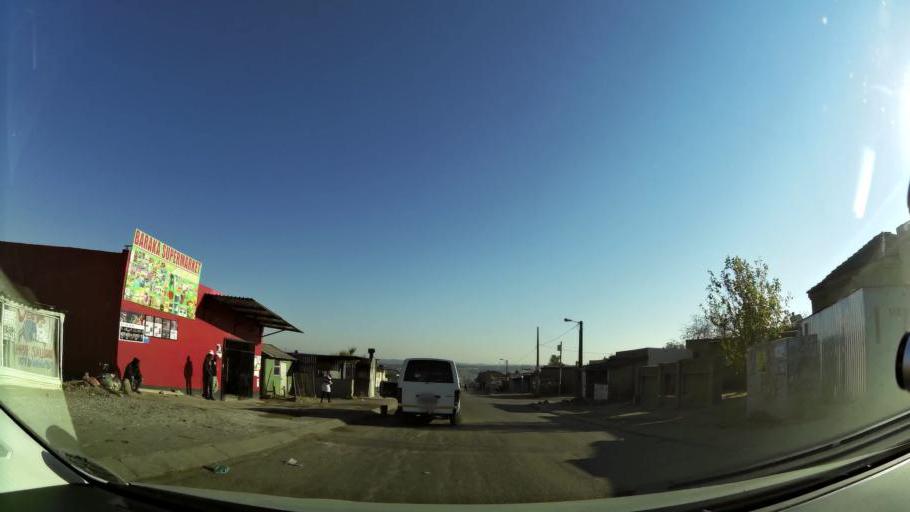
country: ZA
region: Gauteng
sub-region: City of Johannesburg Metropolitan Municipality
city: Modderfontein
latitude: -26.0463
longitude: 28.1580
